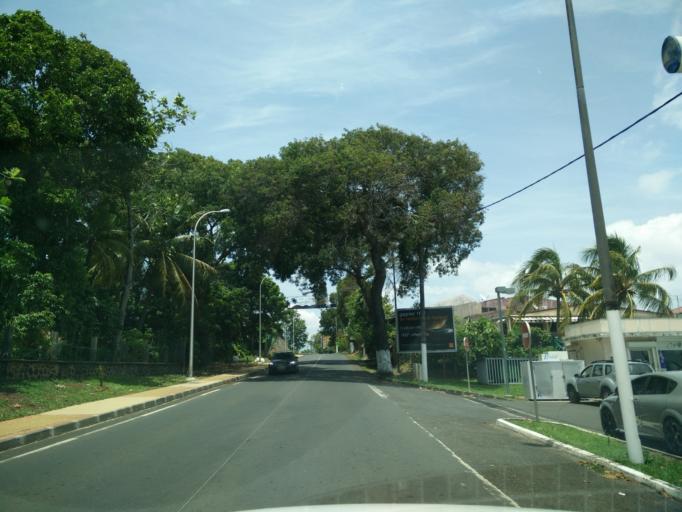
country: GP
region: Guadeloupe
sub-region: Guadeloupe
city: Petit-Bourg
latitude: 16.1965
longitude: -61.5963
